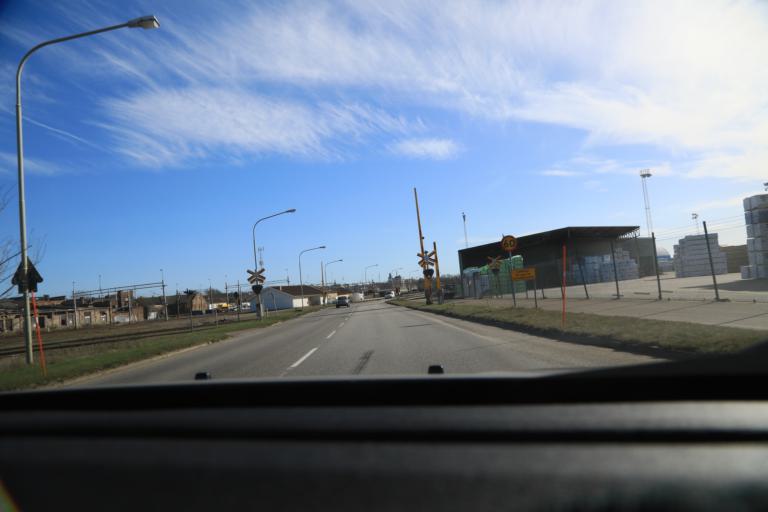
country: SE
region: Halland
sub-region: Varbergs Kommun
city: Varberg
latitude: 57.1155
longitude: 12.2482
